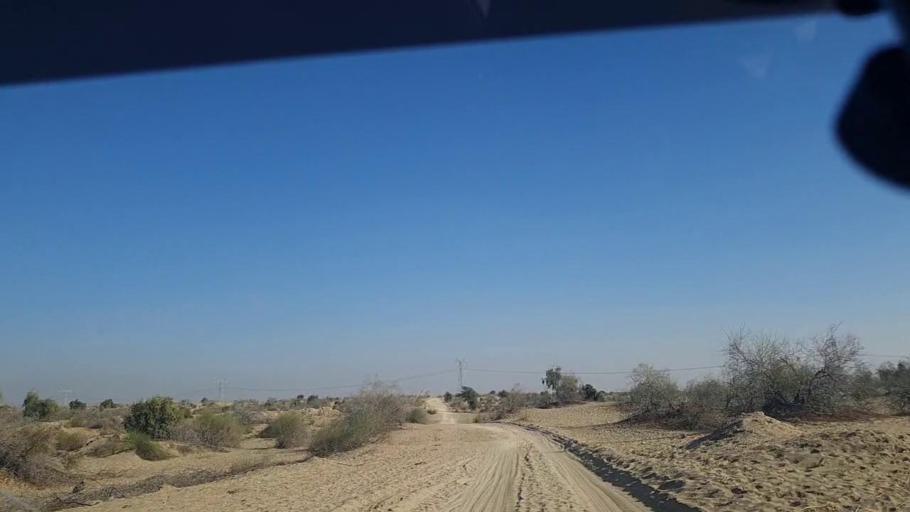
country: PK
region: Sindh
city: Khanpur
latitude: 27.6469
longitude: 69.3965
